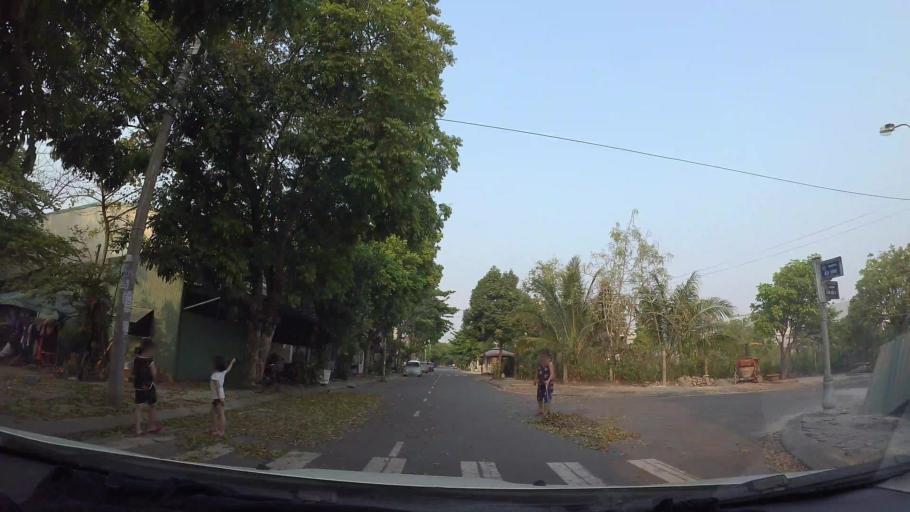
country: VN
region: Da Nang
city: Cam Le
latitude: 16.0199
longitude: 108.1984
